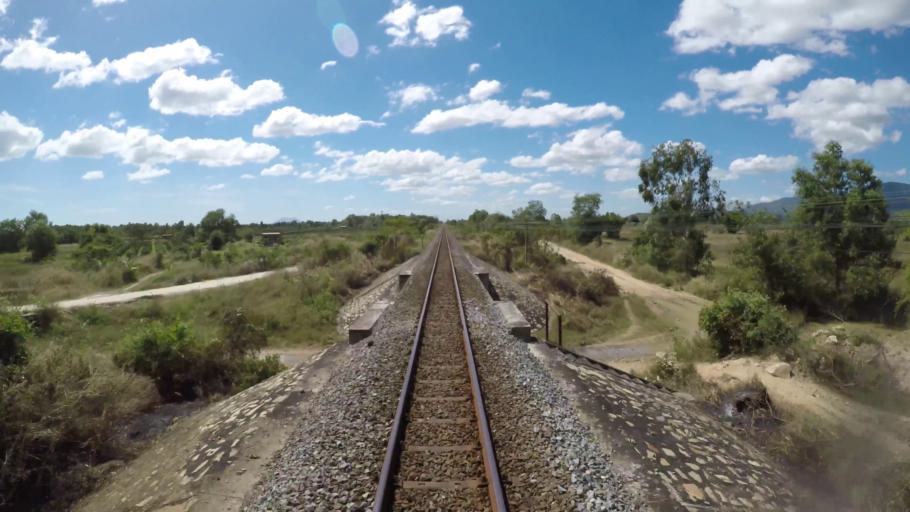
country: VN
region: Binh Thuan
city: Ma Lam
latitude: 11.0310
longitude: 108.0735
